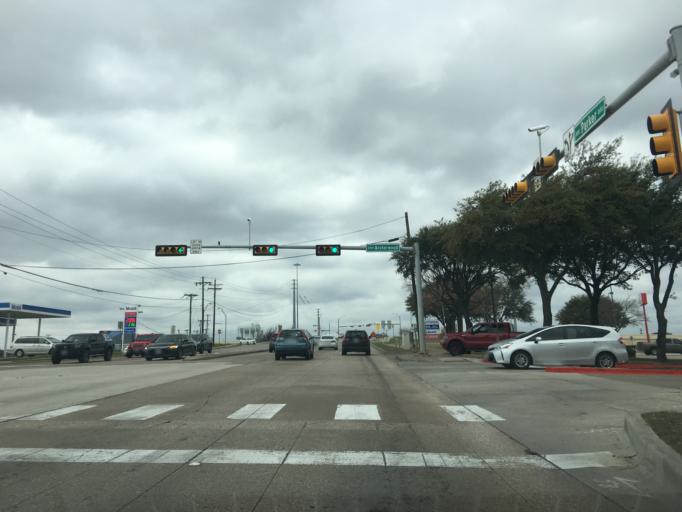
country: US
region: Texas
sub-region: Collin County
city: Plano
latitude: 33.0374
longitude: -96.7016
